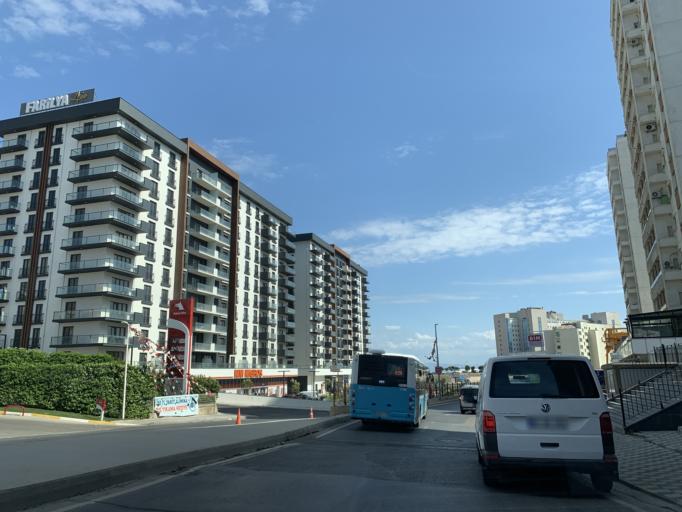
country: TR
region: Istanbul
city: Pendik
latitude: 40.8909
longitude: 29.2629
